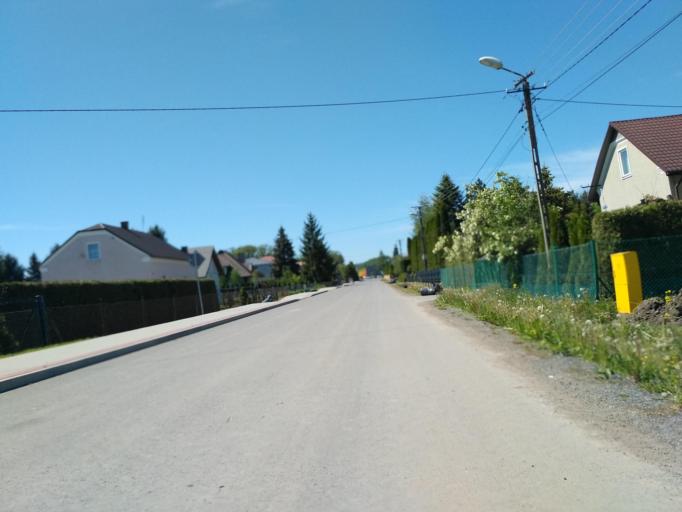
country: PL
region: Subcarpathian Voivodeship
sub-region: Powiat sanocki
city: Besko
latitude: 49.5968
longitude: 21.9670
